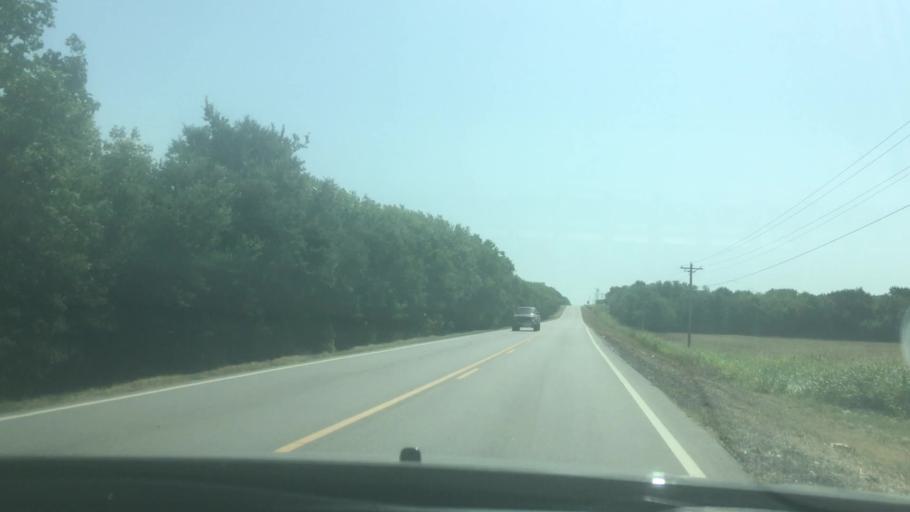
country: US
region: Oklahoma
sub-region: Bryan County
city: Durant
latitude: 34.1428
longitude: -96.3802
